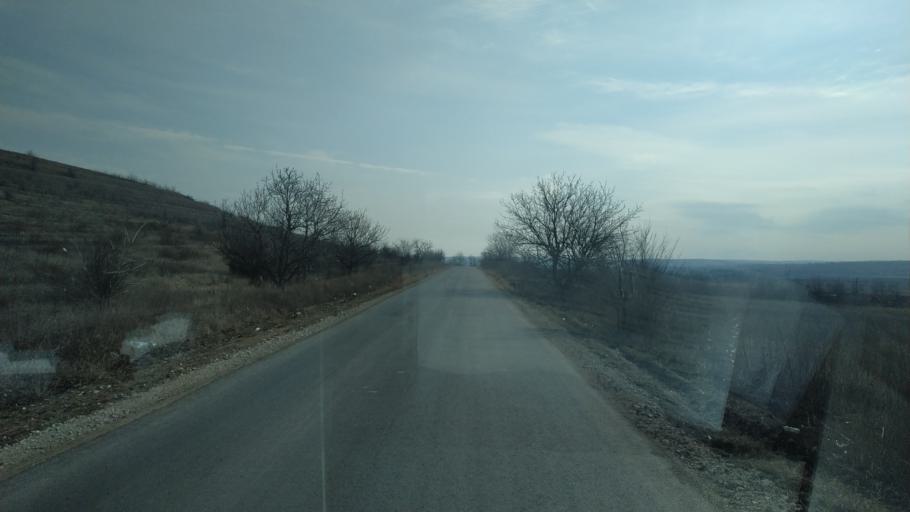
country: MD
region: Chisinau
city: Singera
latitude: 46.9213
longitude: 29.0953
